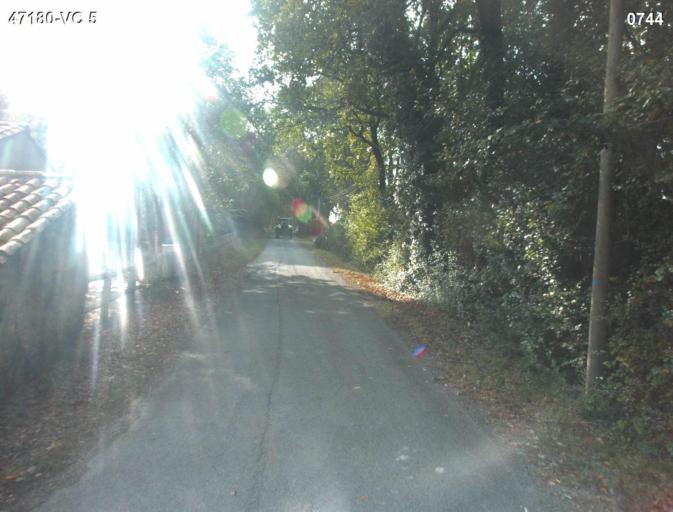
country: FR
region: Aquitaine
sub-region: Departement du Lot-et-Garonne
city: Sainte-Colombe-en-Bruilhois
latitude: 44.1763
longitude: 0.4678
